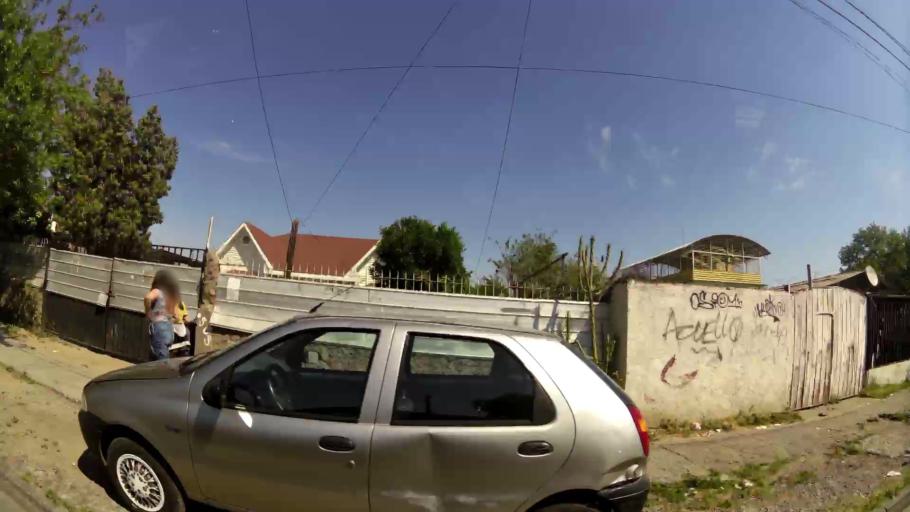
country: CL
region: Santiago Metropolitan
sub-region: Provincia de Santiago
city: La Pintana
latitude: -33.5443
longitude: -70.6256
